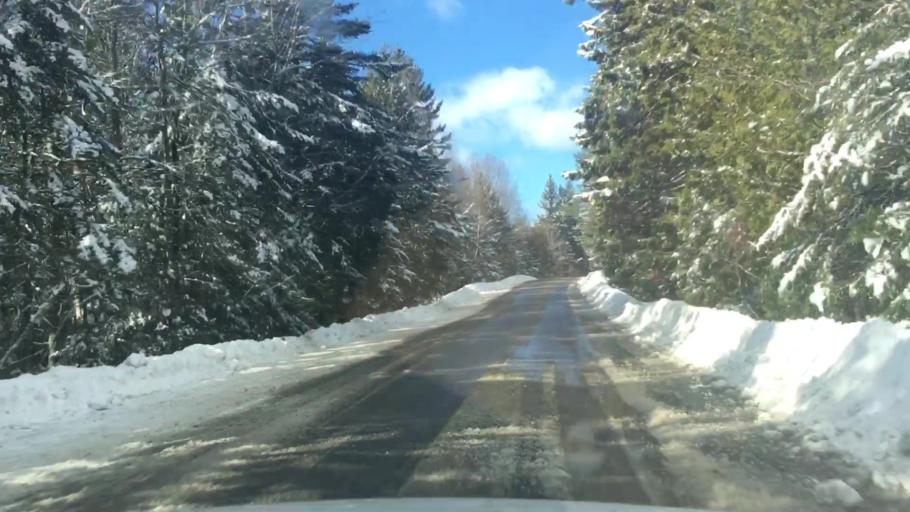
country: US
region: Maine
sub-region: Washington County
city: Machias
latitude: 44.6848
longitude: -67.4590
